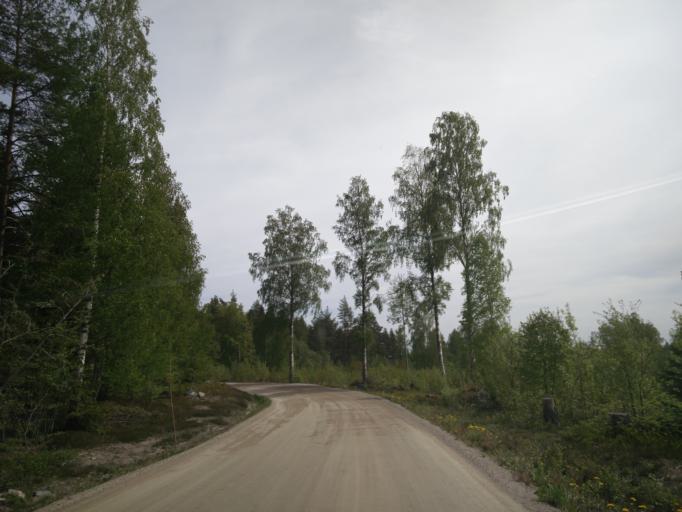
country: SE
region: Gaevleborg
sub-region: Hudiksvalls Kommun
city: Sorforsa
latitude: 61.7382
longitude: 16.9552
